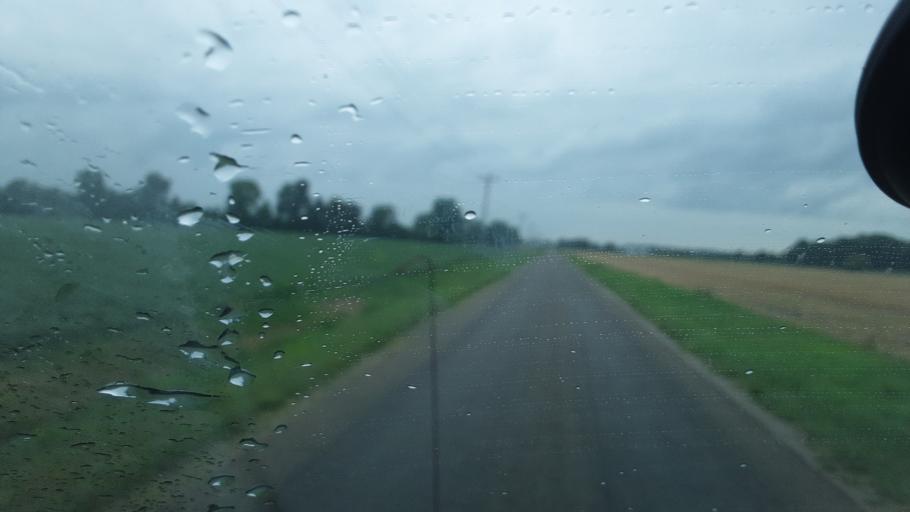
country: US
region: Ohio
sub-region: Defiance County
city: Hicksville
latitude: 41.3249
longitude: -84.6697
